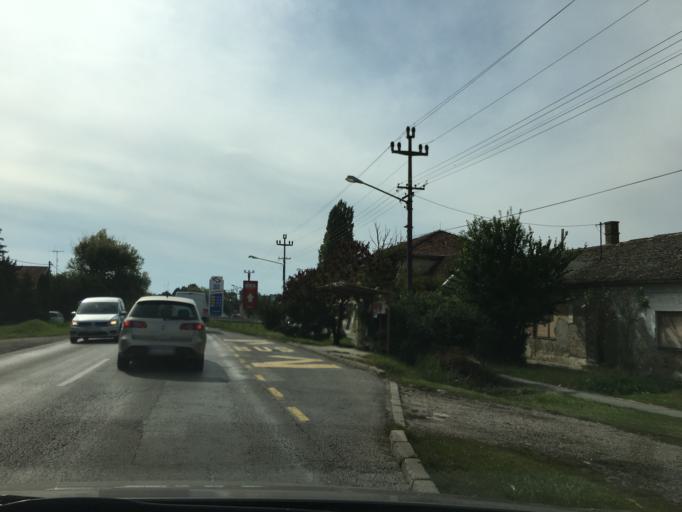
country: RS
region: Autonomna Pokrajina Vojvodina
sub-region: Juznobacki Okrug
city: Temerin
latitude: 45.4222
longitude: 19.8937
